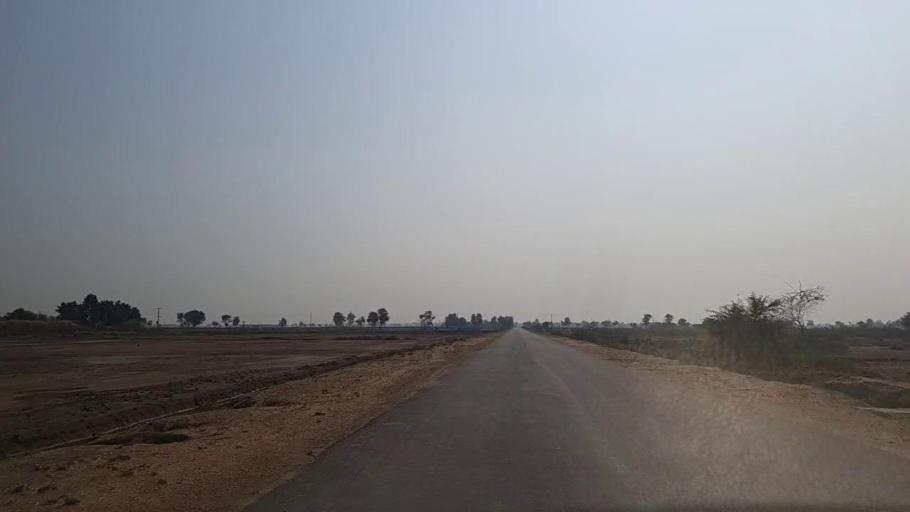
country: PK
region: Sindh
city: Jam Sahib
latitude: 26.3561
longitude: 68.5346
